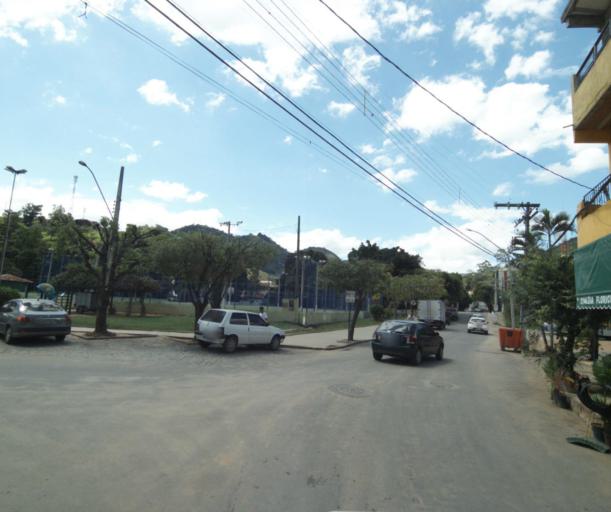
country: BR
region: Espirito Santo
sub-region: Mimoso Do Sul
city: Mimoso do Sul
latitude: -21.0638
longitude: -41.3658
